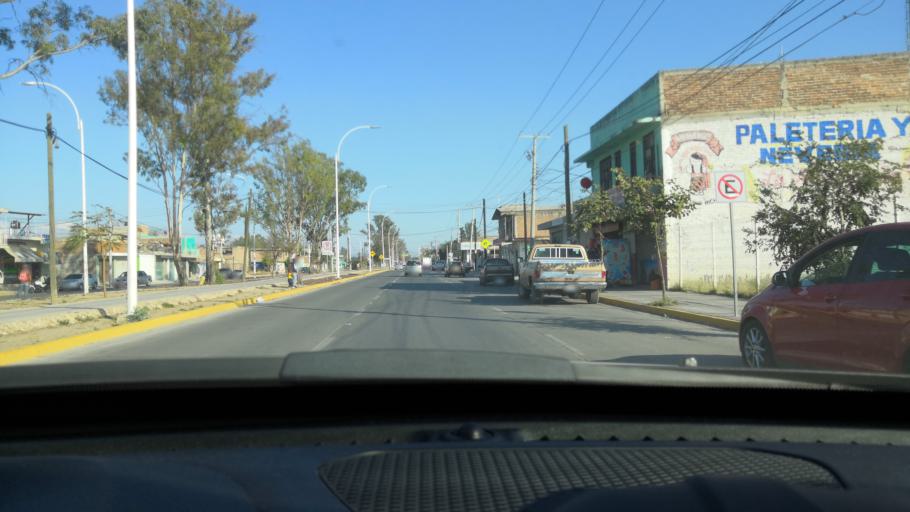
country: MX
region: Guanajuato
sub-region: Leon
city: San Jose de Duran (Los Troncoso)
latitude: 21.0619
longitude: -101.6207
